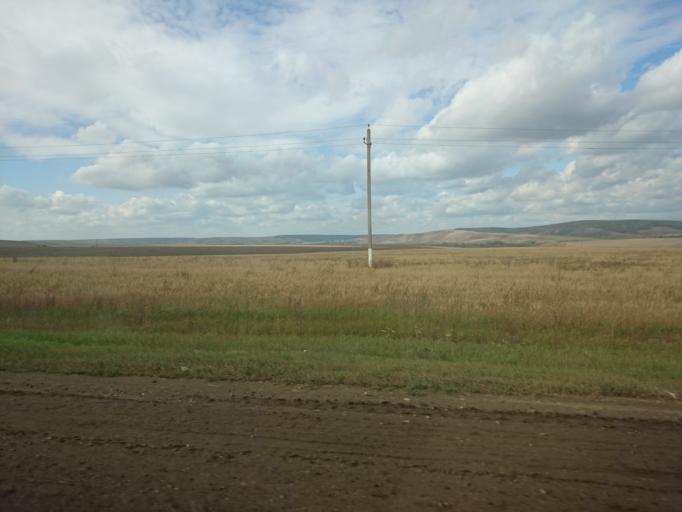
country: RU
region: Samara
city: Kamyshla
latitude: 54.0692
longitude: 52.1740
